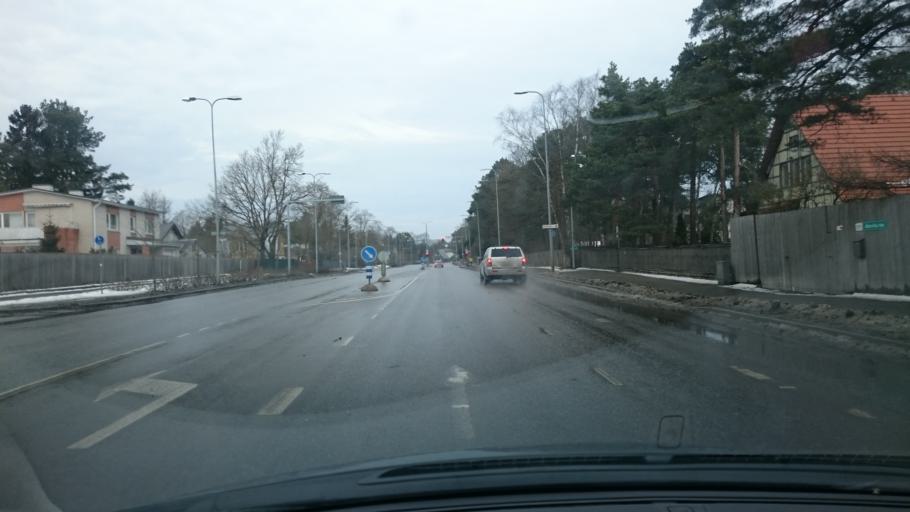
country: EE
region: Harju
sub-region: Tallinna linn
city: Tallinn
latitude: 59.3834
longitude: 24.7176
